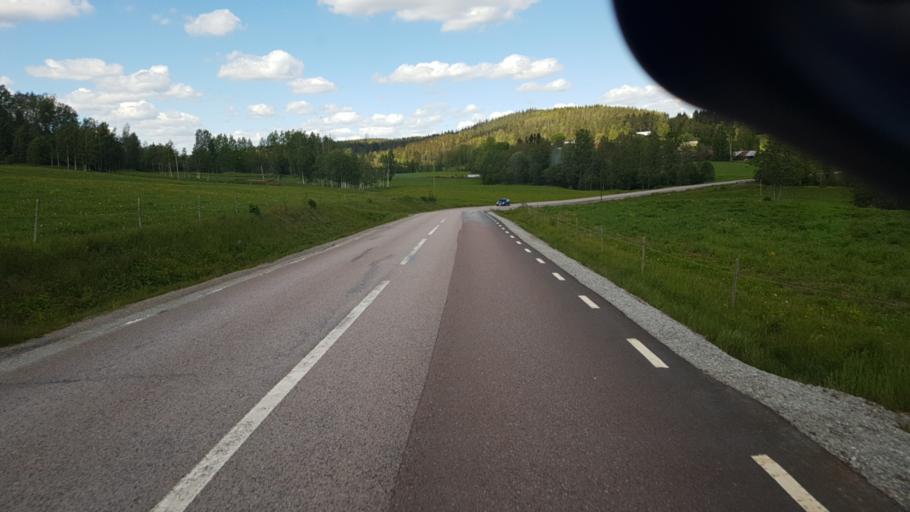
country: SE
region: Vaermland
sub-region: Sunne Kommun
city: Sunne
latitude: 59.6654
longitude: 13.0082
